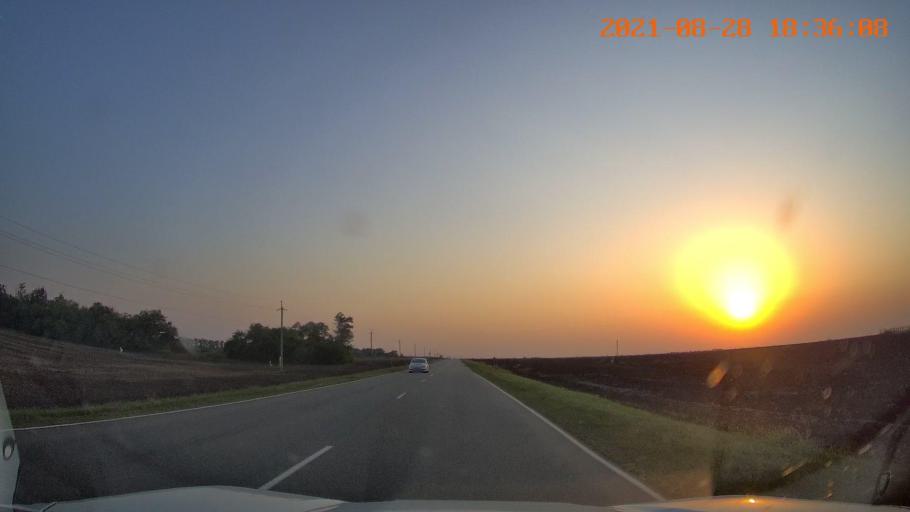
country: RU
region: Adygeya
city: Giaginskaya
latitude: 44.8686
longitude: 40.1187
